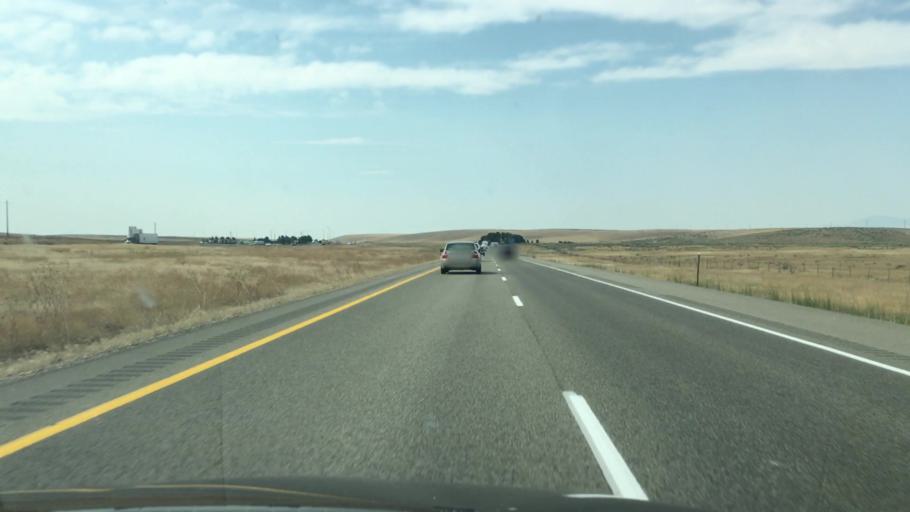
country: US
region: Idaho
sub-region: Ada County
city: Boise
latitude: 43.4711
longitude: -116.0988
